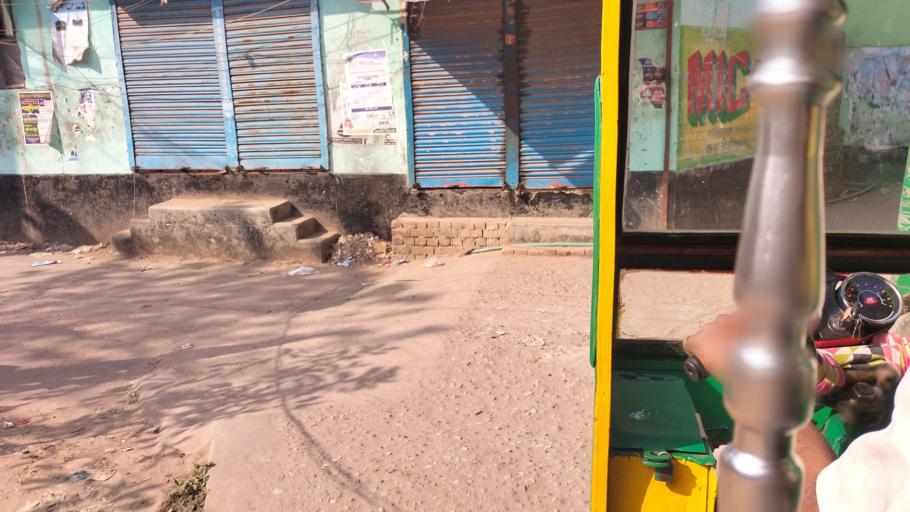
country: BD
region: Dhaka
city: Azimpur
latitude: 23.7952
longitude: 90.3374
